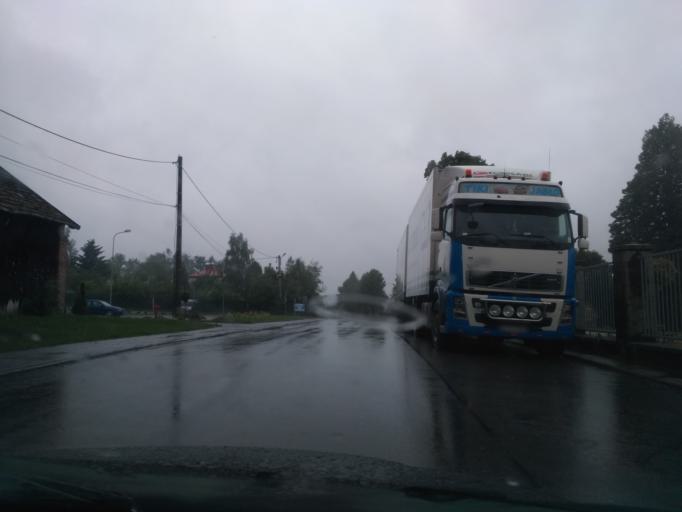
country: PL
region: Subcarpathian Voivodeship
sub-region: Powiat jasielski
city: Debowiec
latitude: 49.6846
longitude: 21.4650
